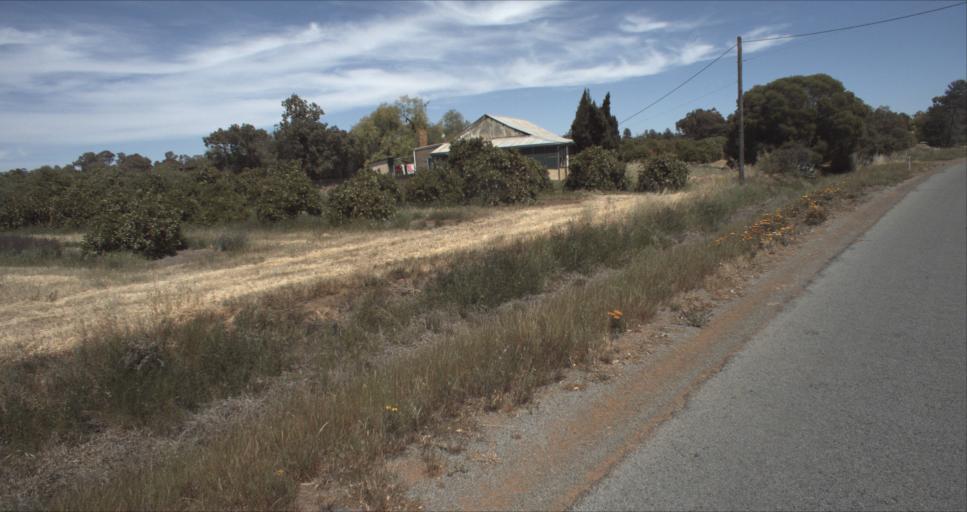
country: AU
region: New South Wales
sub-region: Leeton
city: Leeton
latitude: -34.5717
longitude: 146.4362
